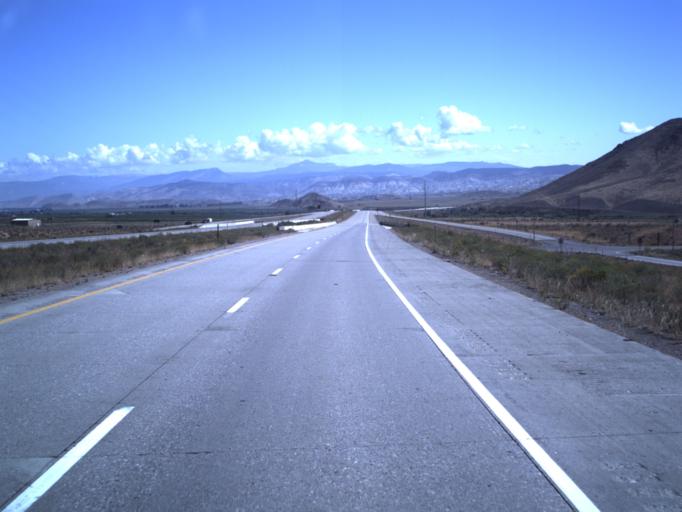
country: US
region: Utah
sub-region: Sevier County
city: Aurora
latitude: 38.8728
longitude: -111.9679
